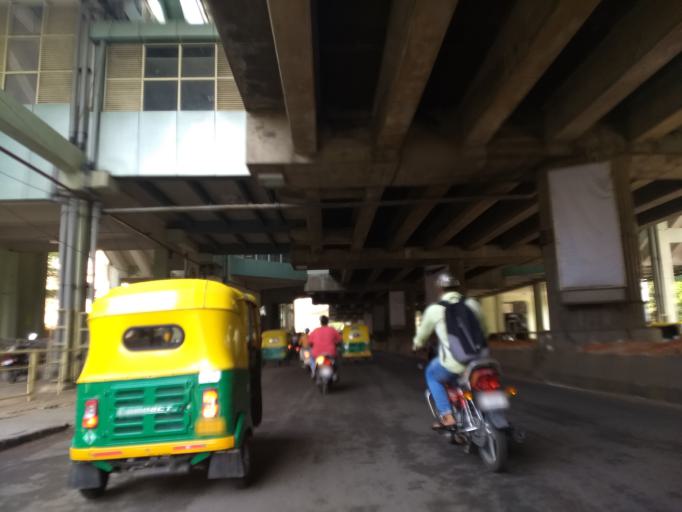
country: IN
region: Karnataka
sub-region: Bangalore Urban
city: Bangalore
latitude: 12.9458
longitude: 77.5799
